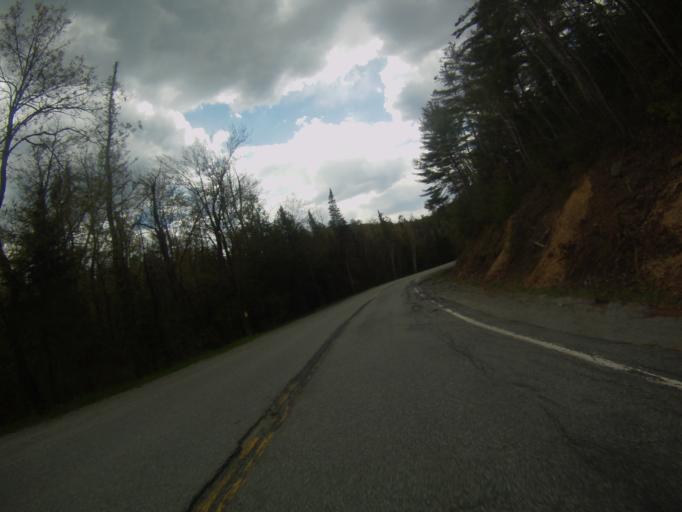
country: US
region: New York
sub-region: Essex County
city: Mineville
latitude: 44.0781
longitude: -73.6203
